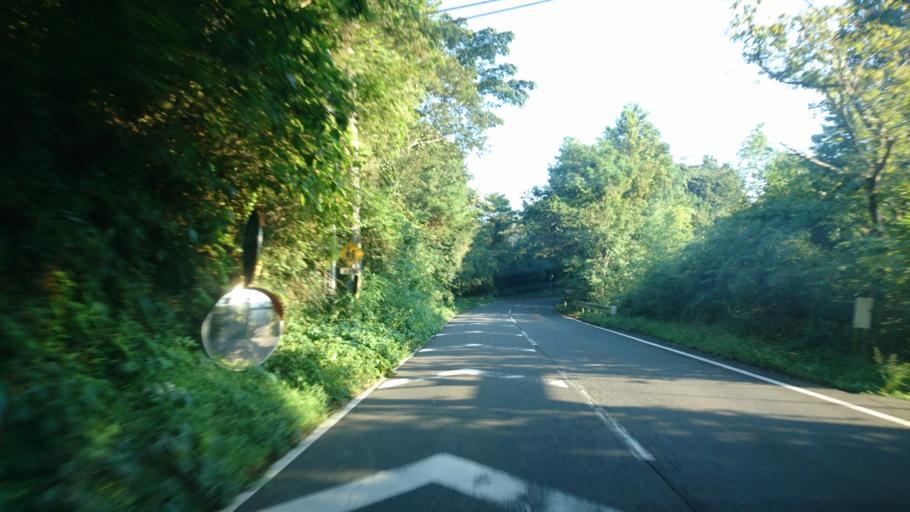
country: JP
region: Chiba
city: Kawaguchi
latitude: 35.1874
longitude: 140.0077
